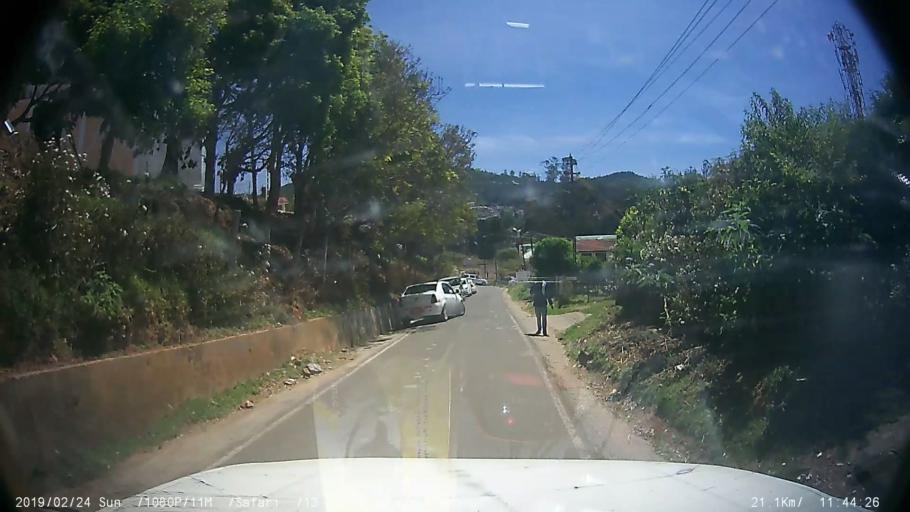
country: IN
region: Tamil Nadu
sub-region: Nilgiri
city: Ooty
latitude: 11.4168
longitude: 76.7080
